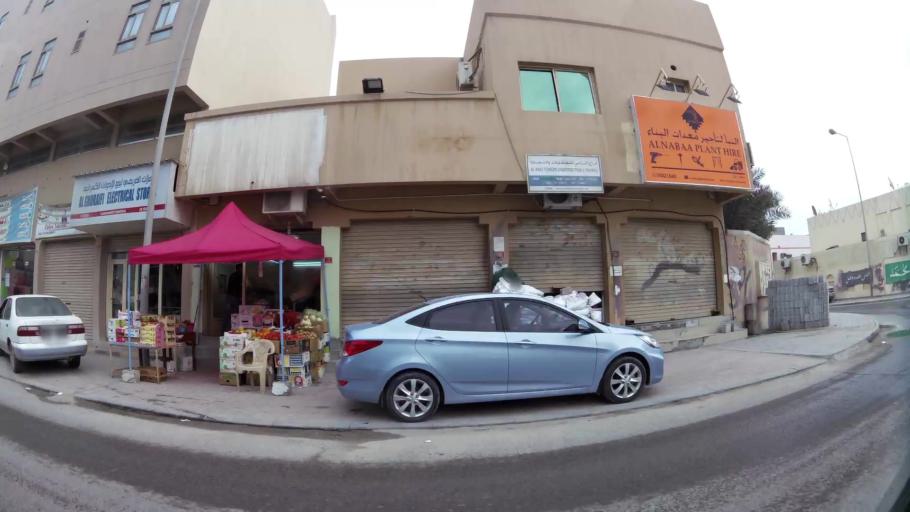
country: BH
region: Northern
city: Sitrah
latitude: 26.1698
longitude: 50.6122
